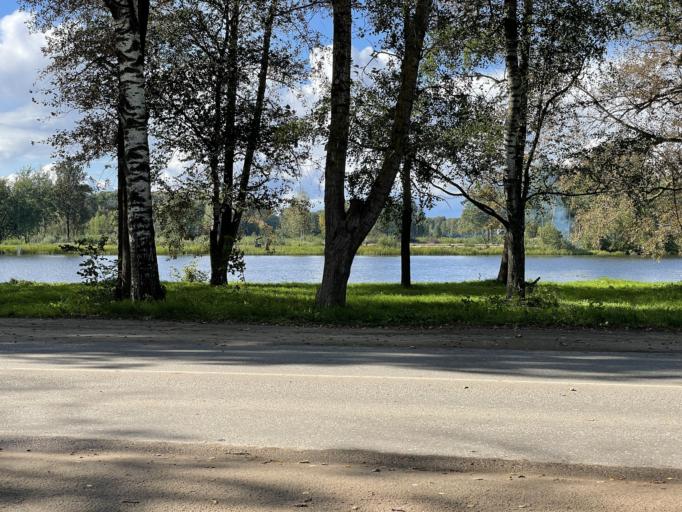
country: RU
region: Tverskaya
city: Vyshniy Volochek
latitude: 57.5778
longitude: 34.5574
